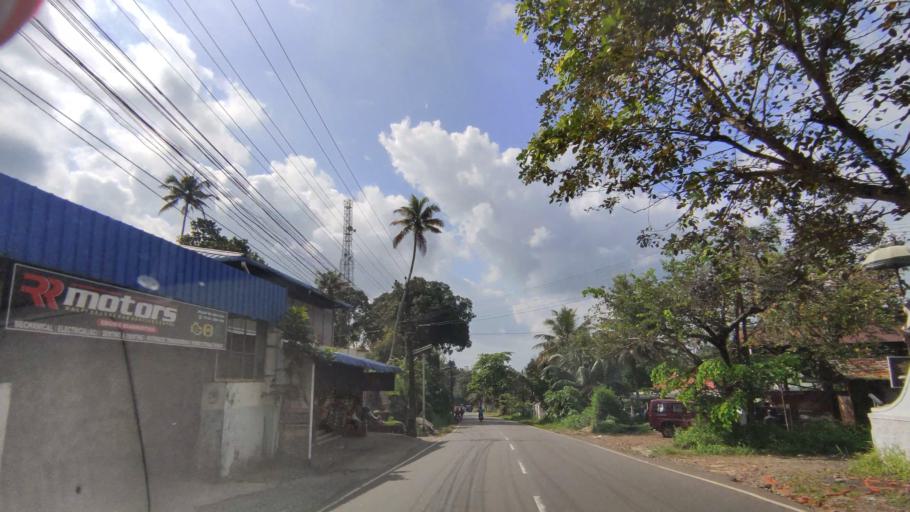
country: IN
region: Kerala
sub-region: Kottayam
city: Kottayam
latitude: 9.6731
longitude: 76.5538
